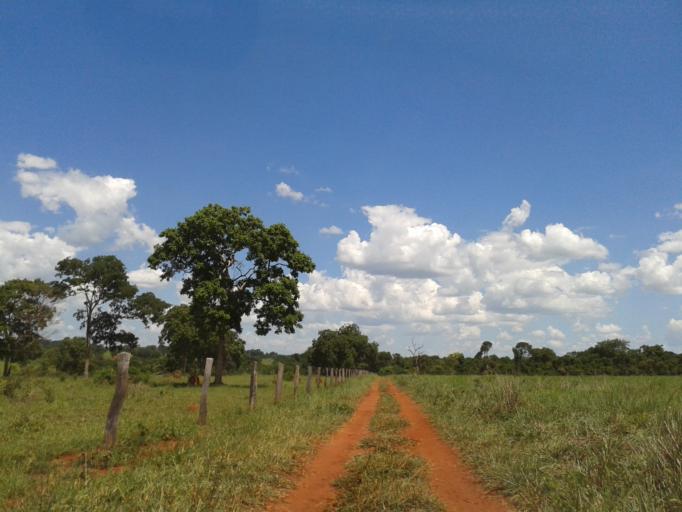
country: BR
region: Minas Gerais
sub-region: Santa Vitoria
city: Santa Vitoria
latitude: -19.1374
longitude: -50.5534
